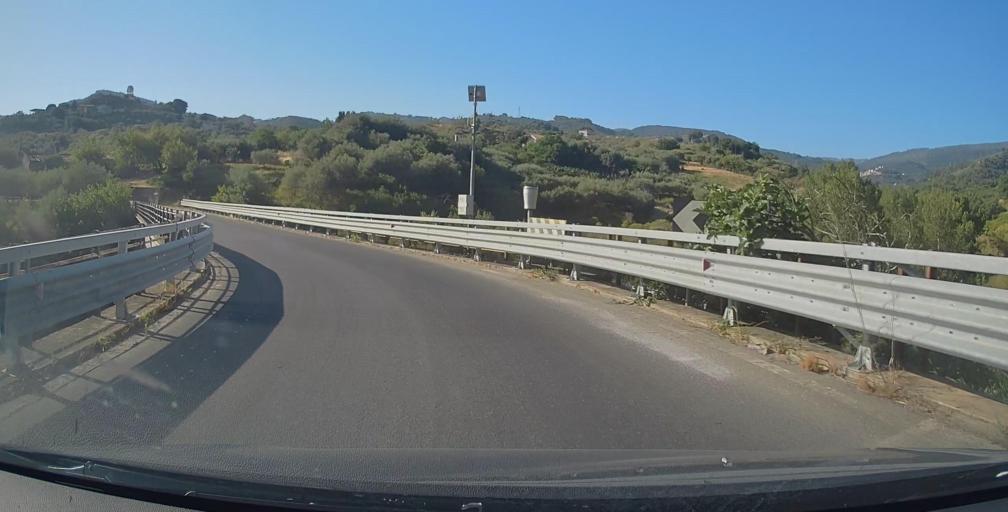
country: IT
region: Sicily
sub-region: Messina
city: Librizzi
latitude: 38.0772
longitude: 14.9720
